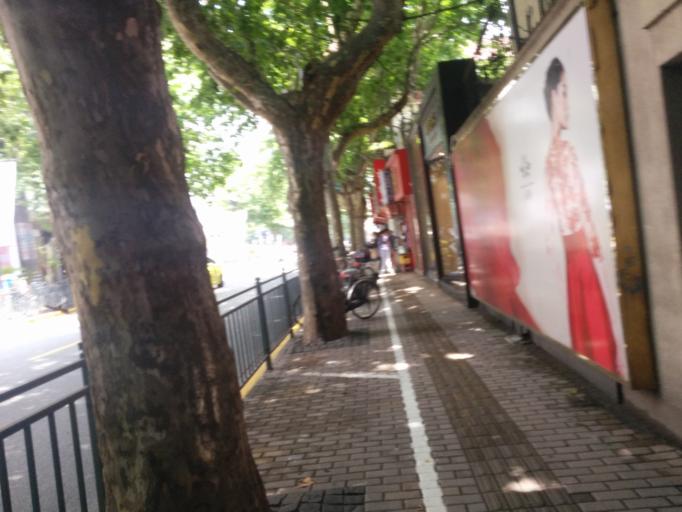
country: CN
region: Shanghai Shi
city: Shanghai
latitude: 31.2189
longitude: 121.4570
